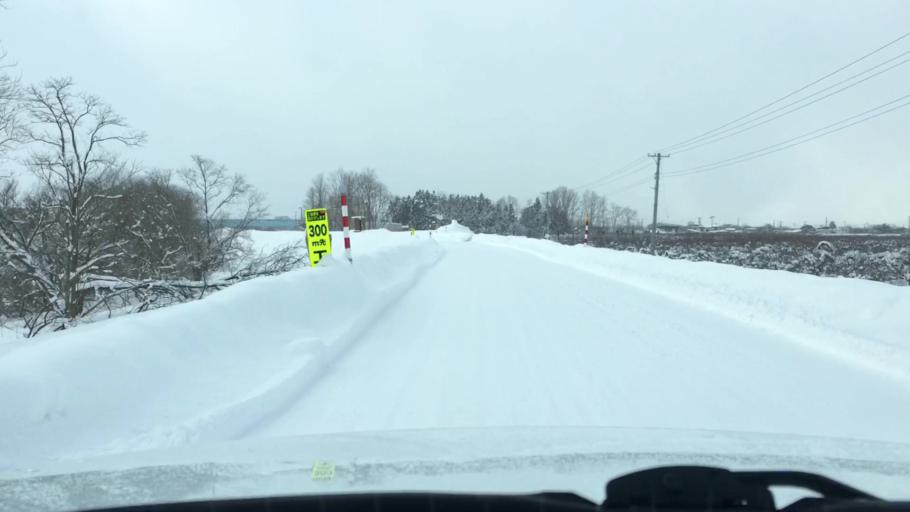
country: JP
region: Aomori
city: Hirosaki
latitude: 40.6531
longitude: 140.4863
